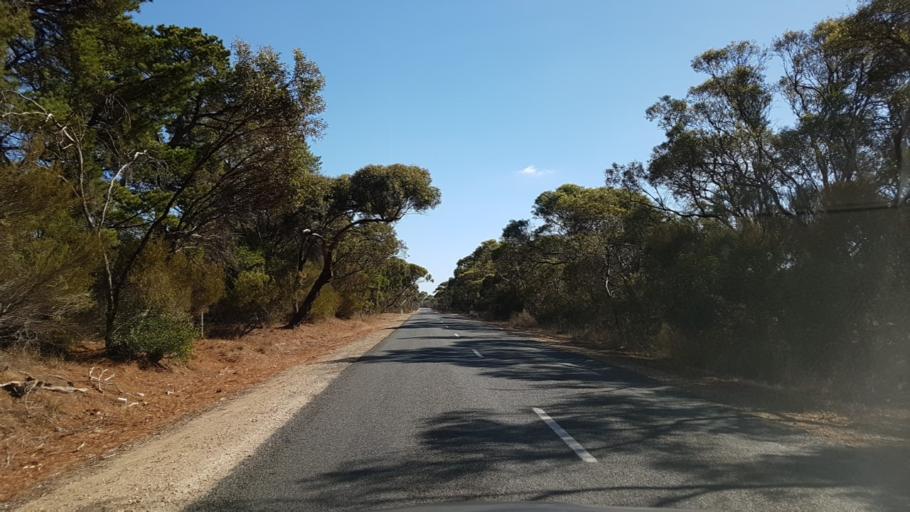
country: AU
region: South Australia
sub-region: Alexandrina
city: Goolwa
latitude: -35.3792
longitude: 138.8216
